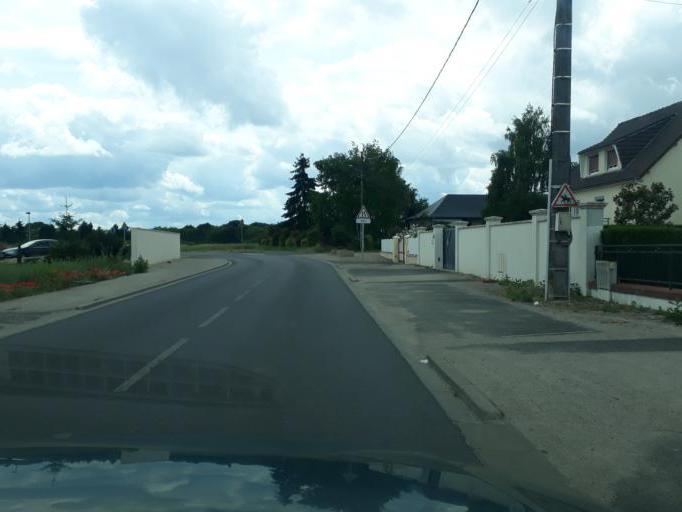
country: FR
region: Centre
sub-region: Departement du Loiret
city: Ingre
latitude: 47.9136
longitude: 1.8165
